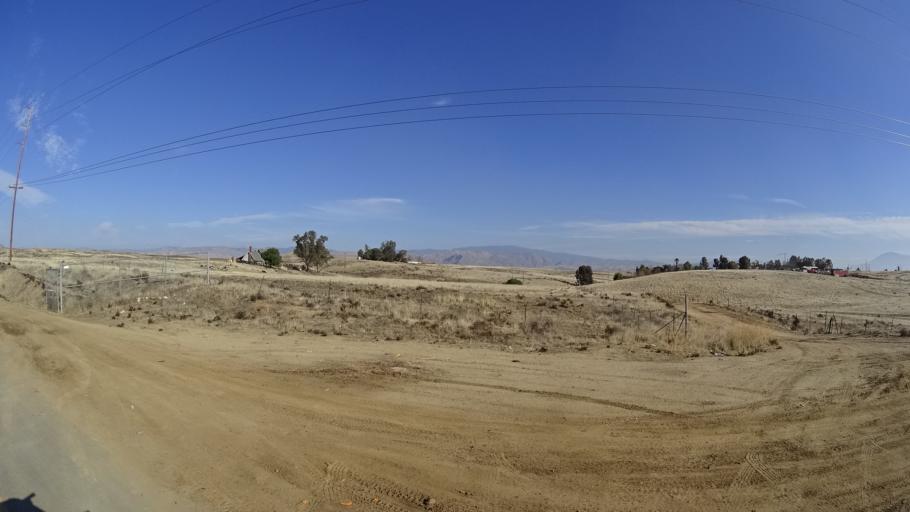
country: US
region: California
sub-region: Kern County
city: Oildale
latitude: 35.4183
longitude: -118.9018
